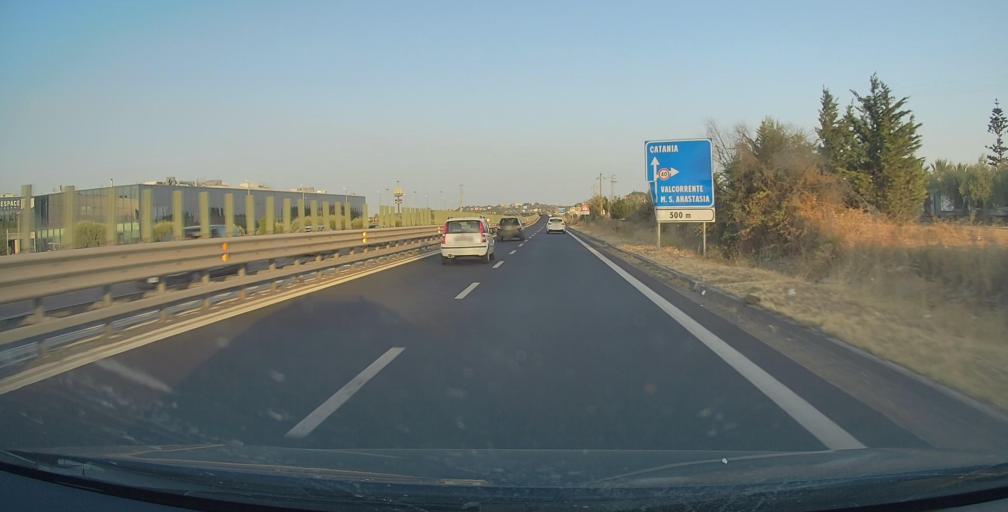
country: IT
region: Sicily
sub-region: Catania
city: Palazzolo
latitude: 37.5425
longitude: 14.9518
